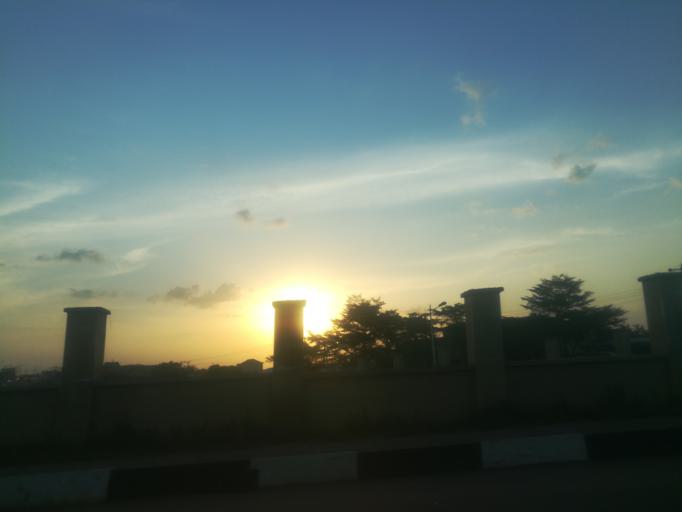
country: NG
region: Ogun
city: Abeokuta
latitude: 7.1484
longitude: 3.3295
